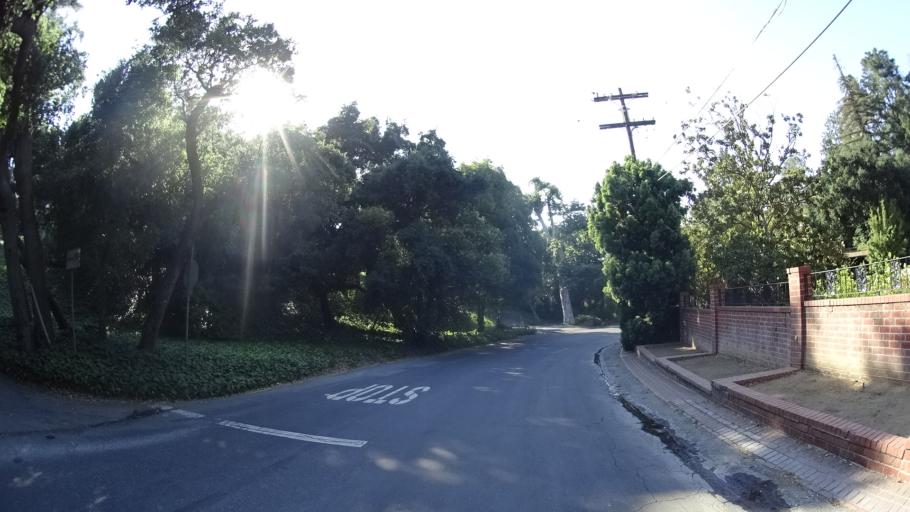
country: US
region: California
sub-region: Los Angeles County
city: Universal City
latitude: 34.1300
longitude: -118.3901
